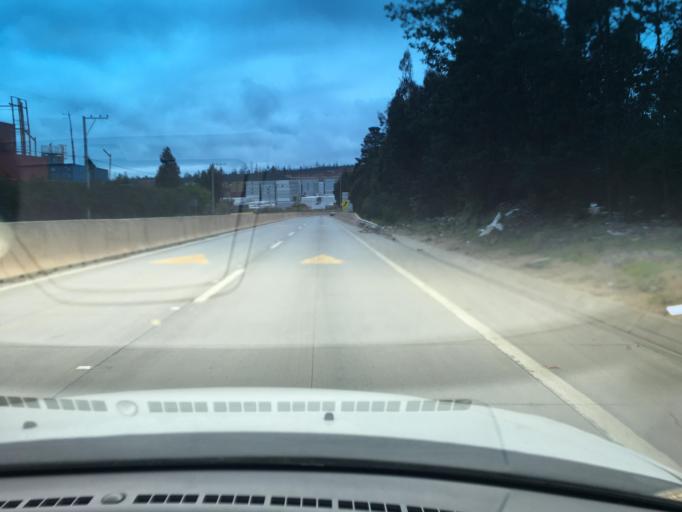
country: CL
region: Valparaiso
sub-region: Provincia de Valparaiso
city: Valparaiso
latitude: -33.0950
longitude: -71.5998
